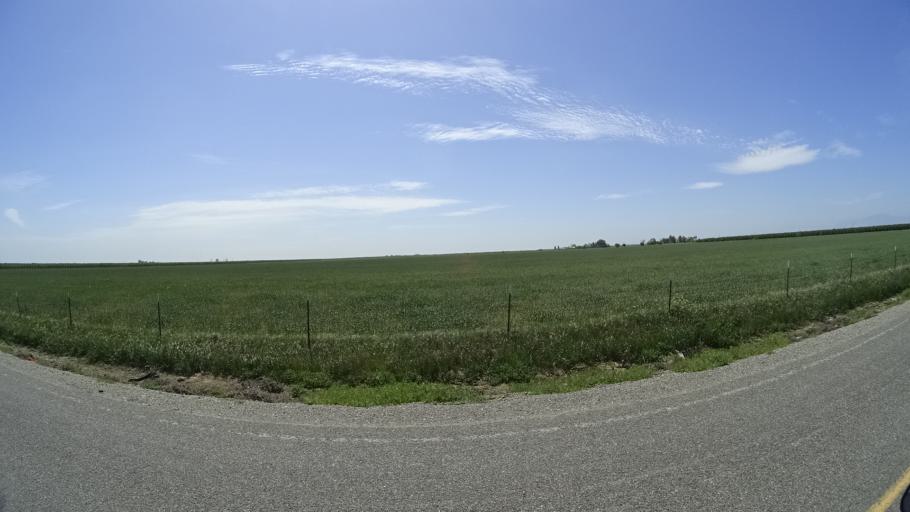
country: US
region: California
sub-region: Glenn County
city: Orland
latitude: 39.6529
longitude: -122.1546
